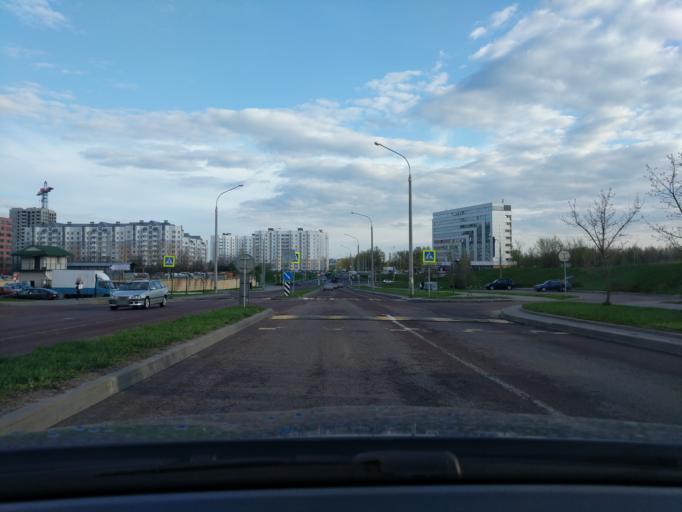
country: BY
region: Minsk
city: Novoye Medvezhino
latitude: 53.9033
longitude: 27.4735
